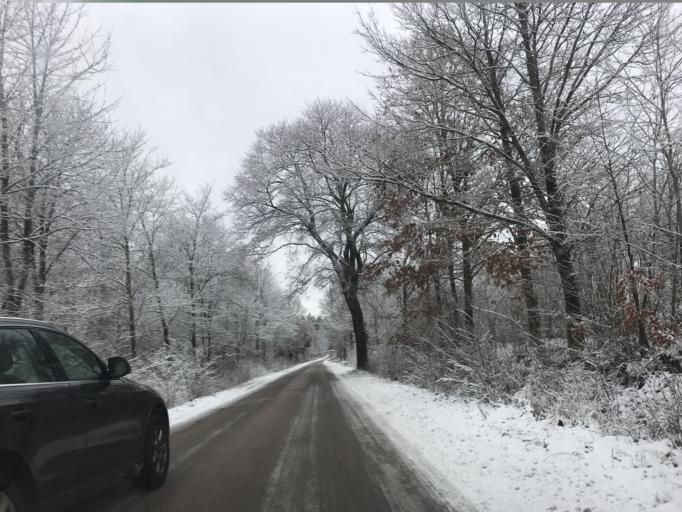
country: PL
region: Pomeranian Voivodeship
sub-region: Powiat bytowski
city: Parchowo
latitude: 54.2378
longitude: 17.5759
